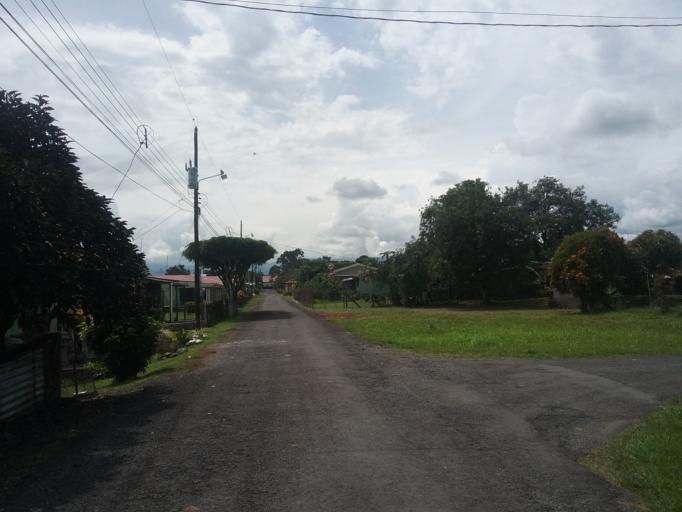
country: CR
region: Limon
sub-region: Canton de Pococi
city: Roxana
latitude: 10.3249
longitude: -83.8861
